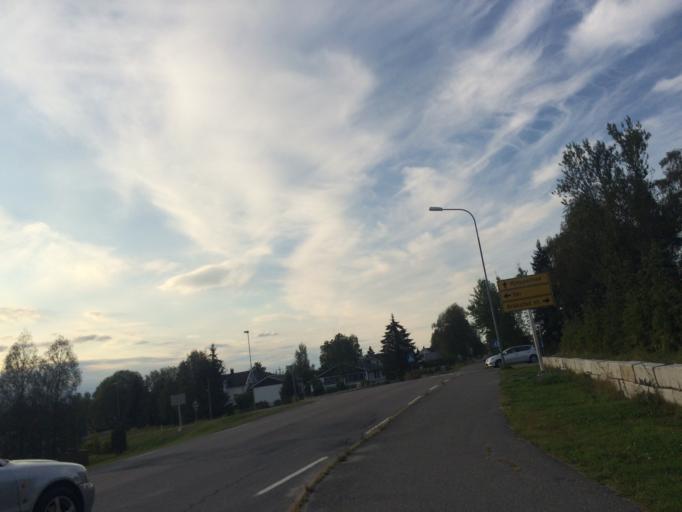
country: NO
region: Akershus
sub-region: Ski
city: Ski
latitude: 59.6808
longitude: 10.8839
